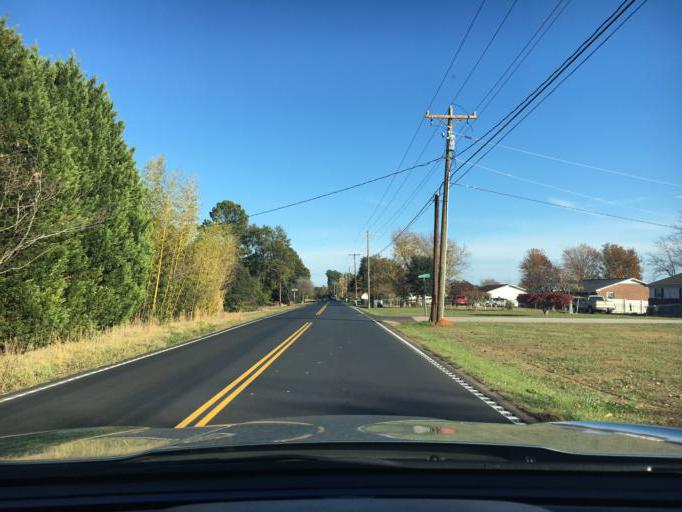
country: US
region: South Carolina
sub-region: Spartanburg County
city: Inman Mills
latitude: 35.0299
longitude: -82.1190
